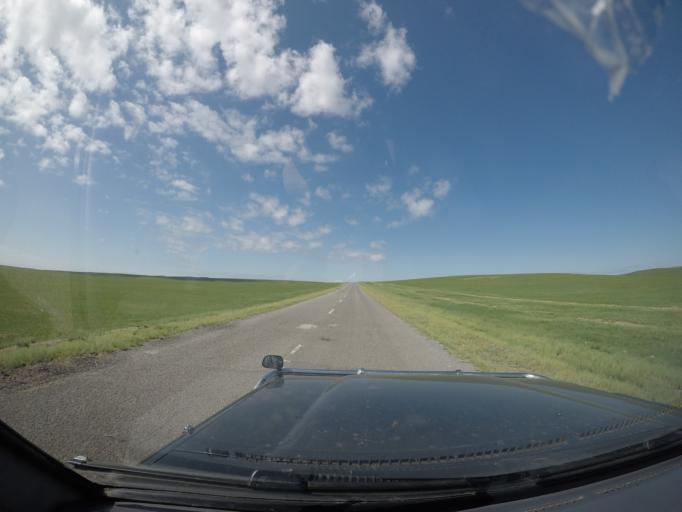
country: MN
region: Suhbaatar
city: Hanhohiy
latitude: 47.3828
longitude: 111.8379
